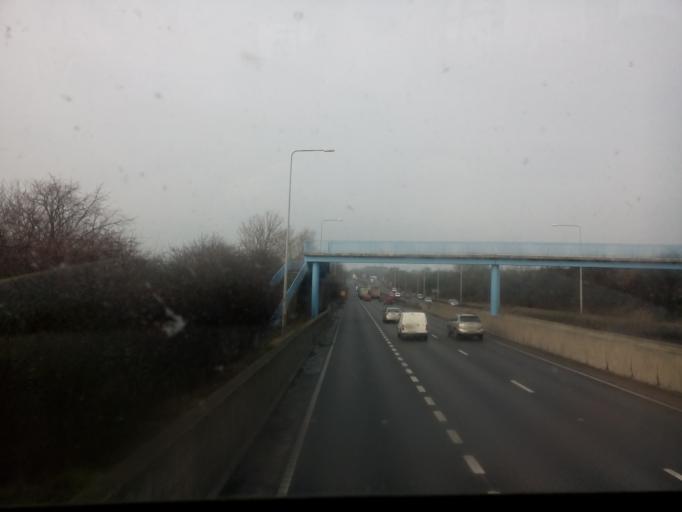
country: GB
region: England
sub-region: Gateshead
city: Lamesley
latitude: 54.9075
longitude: -1.5713
